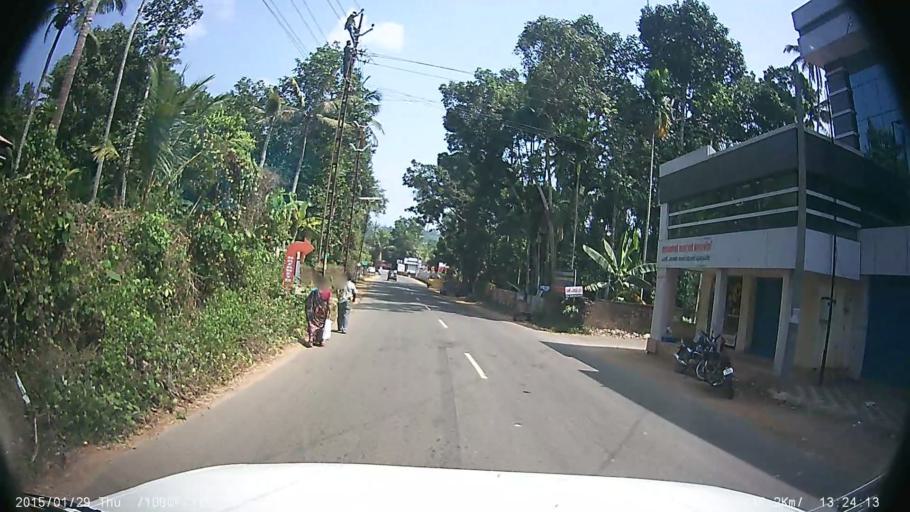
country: IN
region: Kerala
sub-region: Kottayam
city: Palackattumala
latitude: 9.7567
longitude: 76.5569
